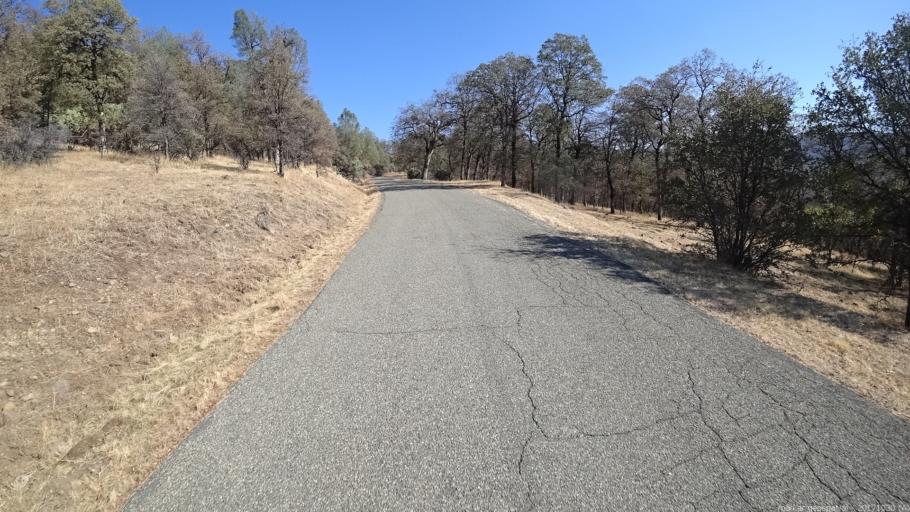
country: US
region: California
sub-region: Shasta County
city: Shingletown
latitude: 40.5735
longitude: -121.8772
